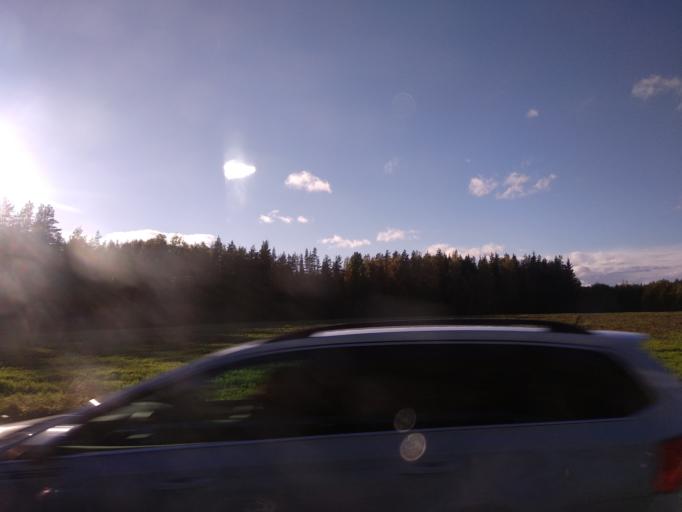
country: EE
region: Polvamaa
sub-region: Polva linn
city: Polva
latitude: 58.0294
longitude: 27.0657
